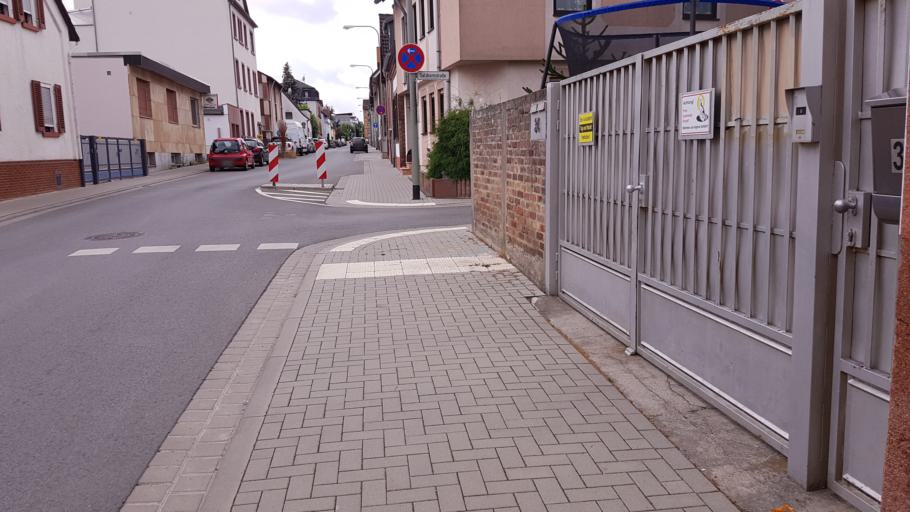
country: DE
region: Hesse
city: Schwalbach am Taunus
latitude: 50.1482
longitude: 8.5328
